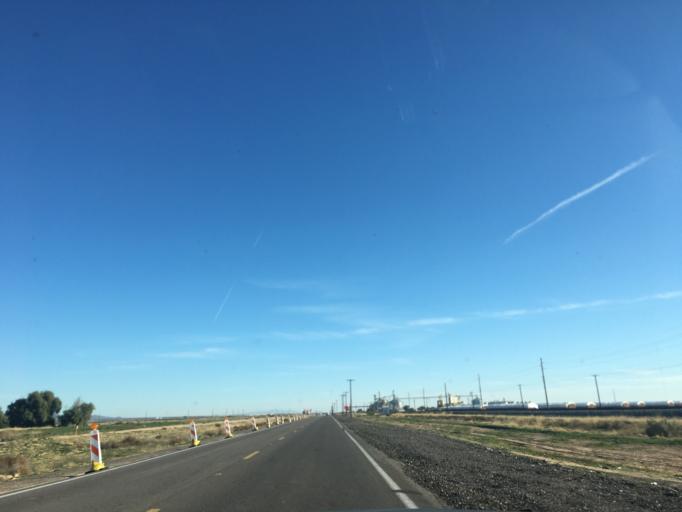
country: US
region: Arizona
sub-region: Pinal County
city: Maricopa
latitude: 33.0220
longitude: -111.9916
